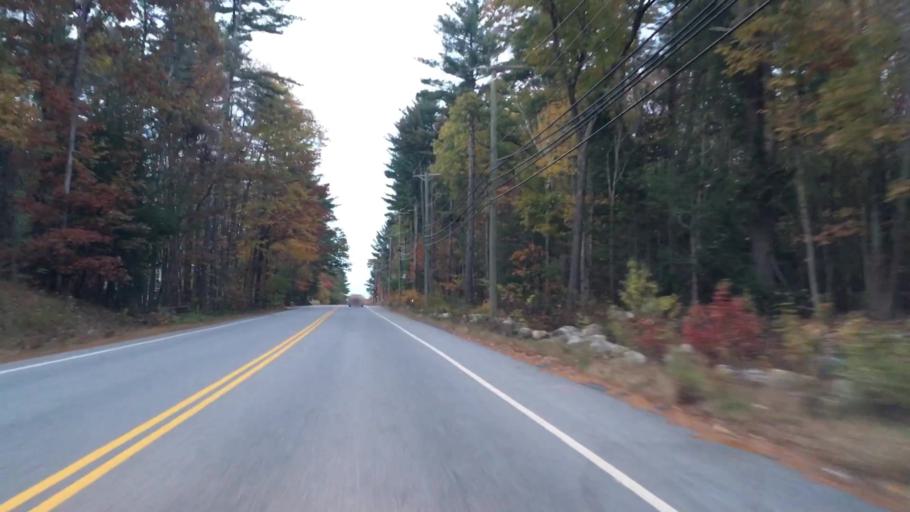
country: US
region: New Hampshire
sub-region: Hillsborough County
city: Milford
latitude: 42.8489
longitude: -71.6354
